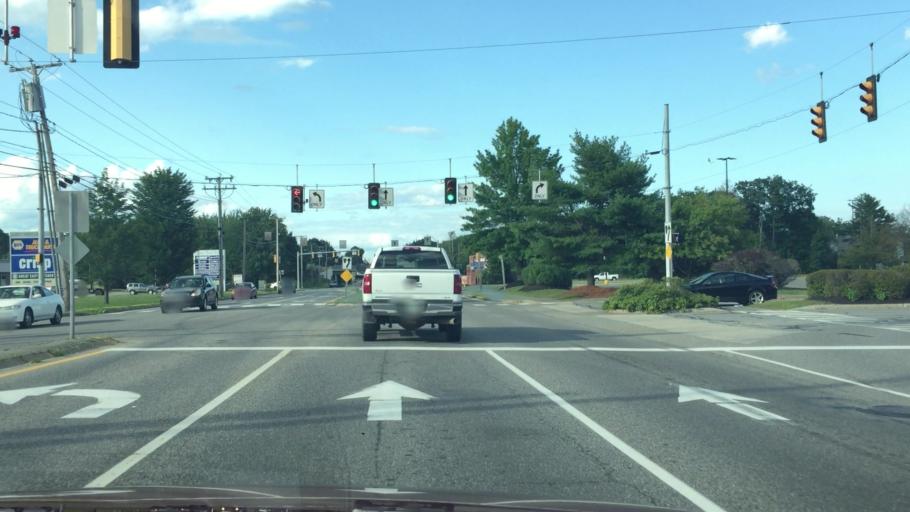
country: US
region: Maine
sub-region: Cumberland County
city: South Portland Gardens
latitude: 43.6231
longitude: -70.3493
